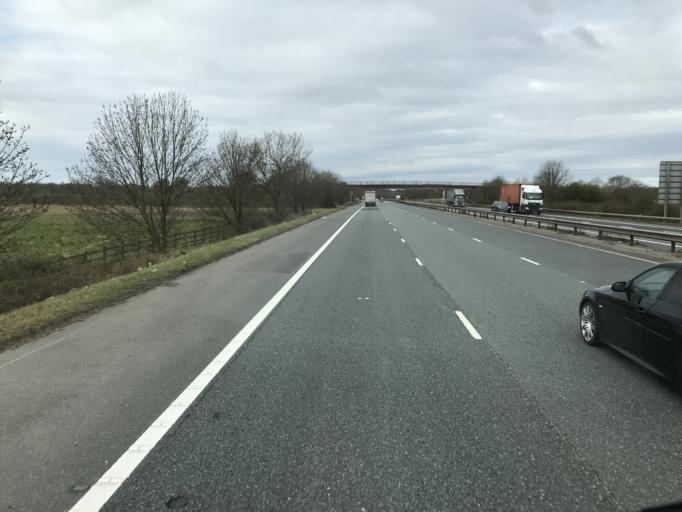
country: GB
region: England
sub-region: Warrington
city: Burtonwood
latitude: 53.4131
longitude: -2.6773
